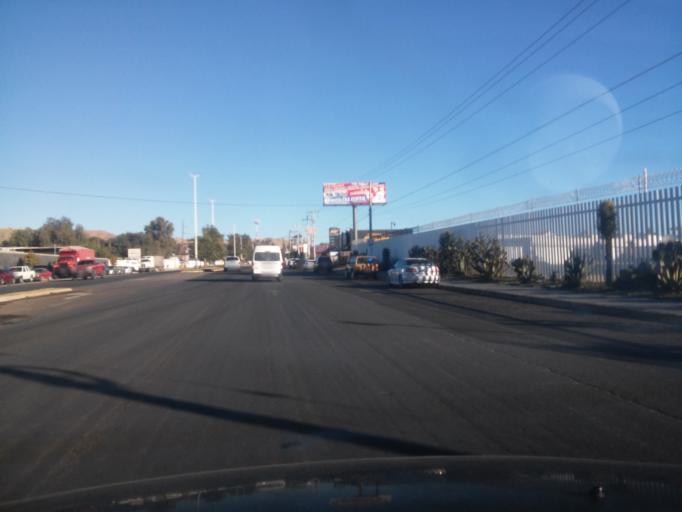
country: MX
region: Durango
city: Victoria de Durango
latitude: 24.0442
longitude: -104.6582
